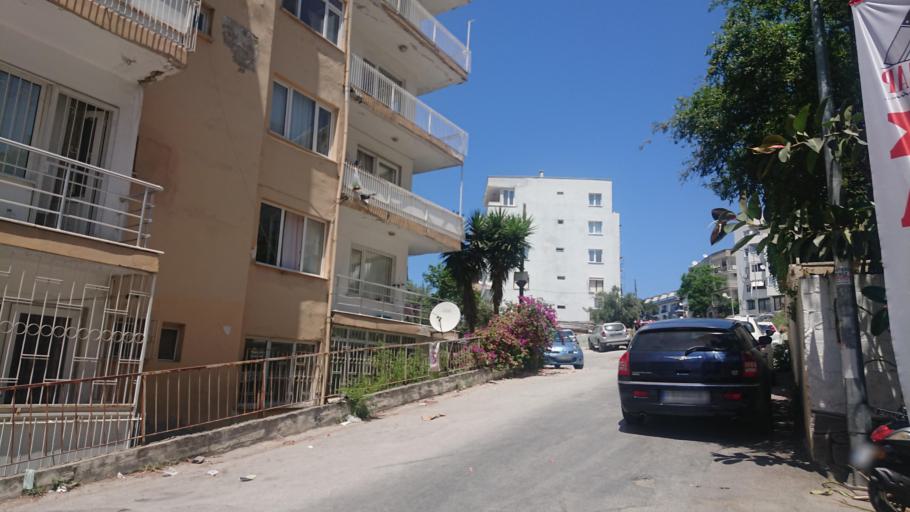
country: TR
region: Aydin
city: Kusadasi
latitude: 37.8633
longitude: 27.2653
